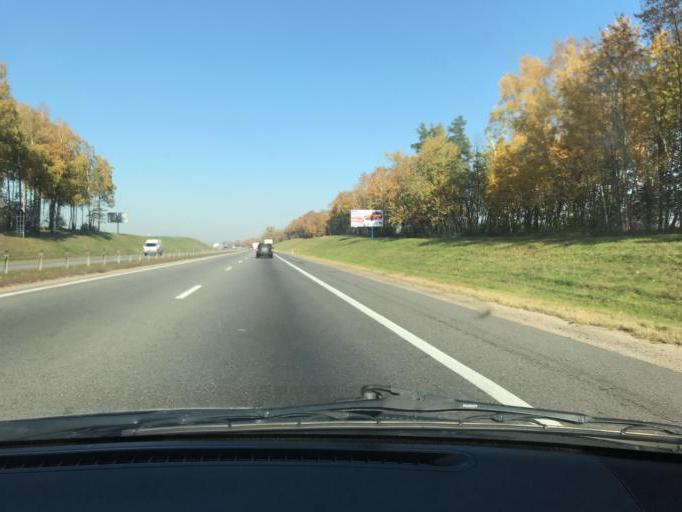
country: BY
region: Minsk
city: Samakhvalavichy
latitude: 53.7644
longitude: 27.5201
